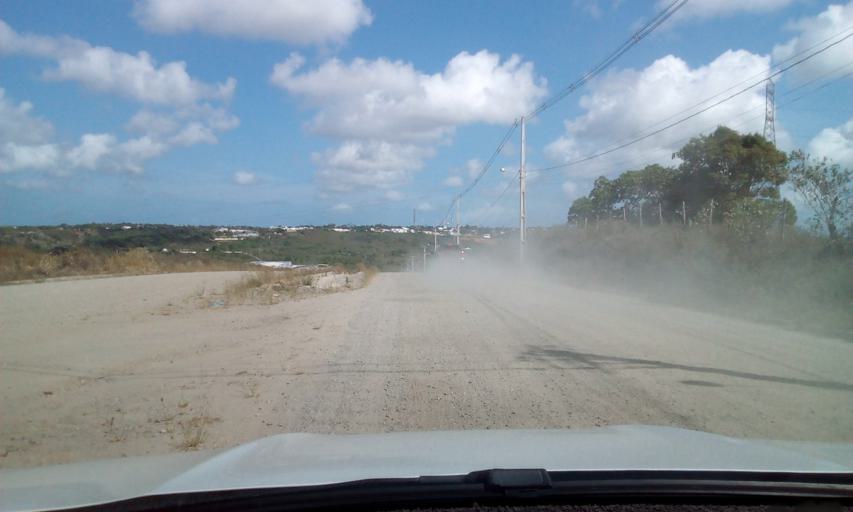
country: BR
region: Paraiba
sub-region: Conde
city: Conde
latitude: -7.2519
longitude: -34.9283
